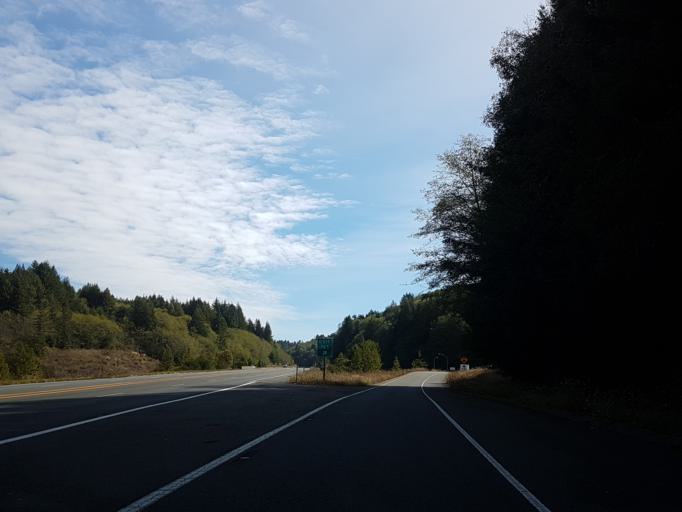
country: US
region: California
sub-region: Del Norte County
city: Bertsch-Oceanview
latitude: 41.4687
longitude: -124.0407
